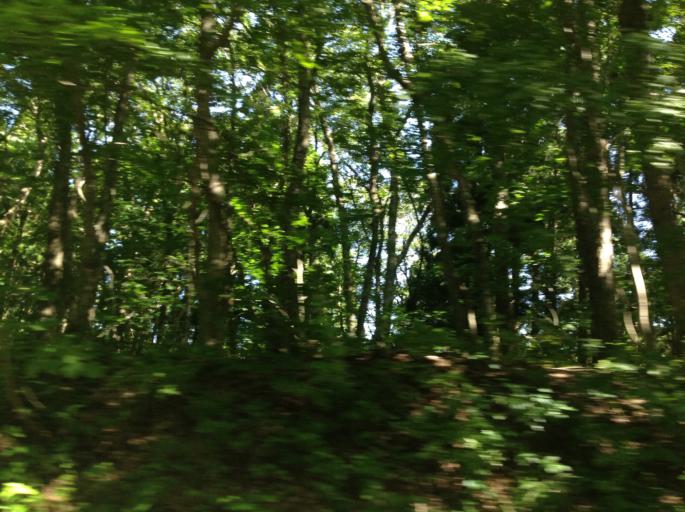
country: JP
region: Akita
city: Kakunodatemachi
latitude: 39.6972
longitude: 140.6650
